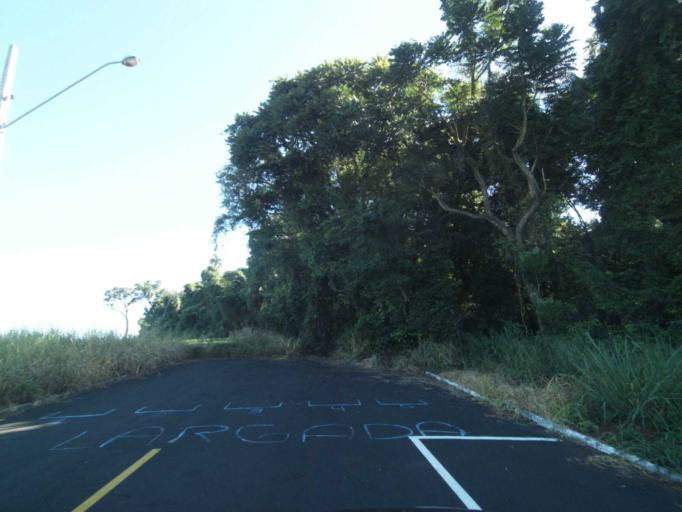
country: BR
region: Parana
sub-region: Coronel Vivida
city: Coronel Vivida
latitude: -25.9715
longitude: -52.8101
